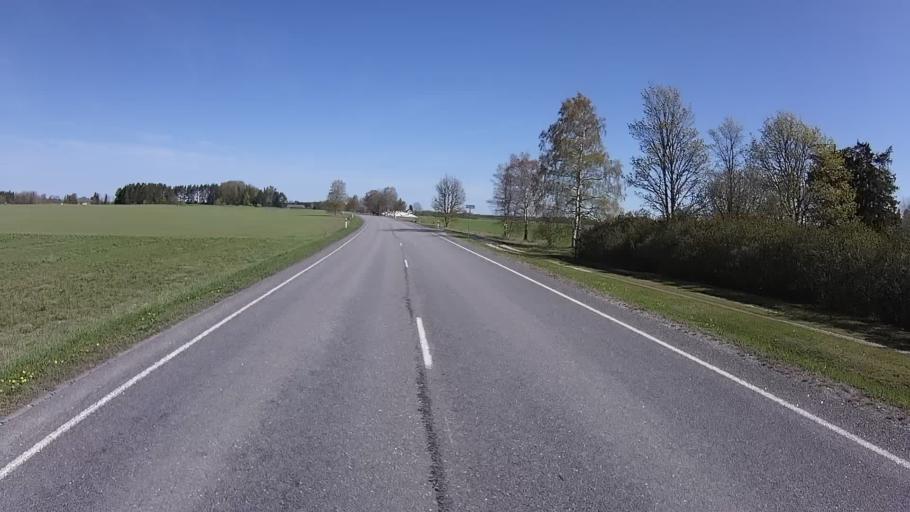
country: EE
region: Raplamaa
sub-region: Kehtna vald
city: Kehtna
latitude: 58.8906
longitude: 24.7883
